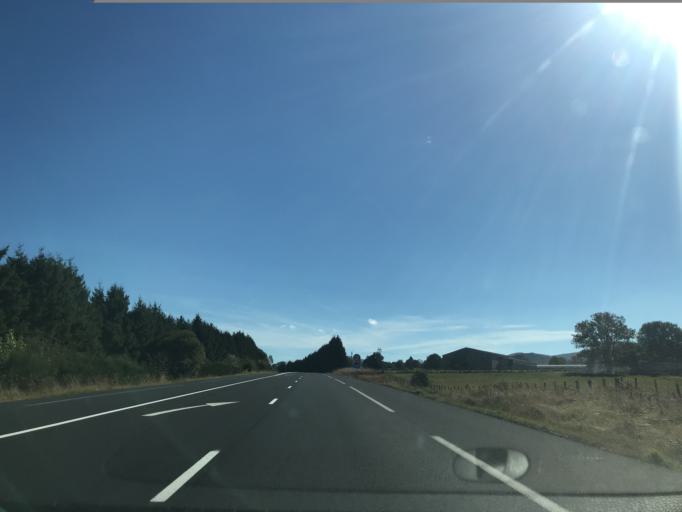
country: FR
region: Auvergne
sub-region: Departement du Puy-de-Dome
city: La Bourboule
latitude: 45.6634
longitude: 2.7486
